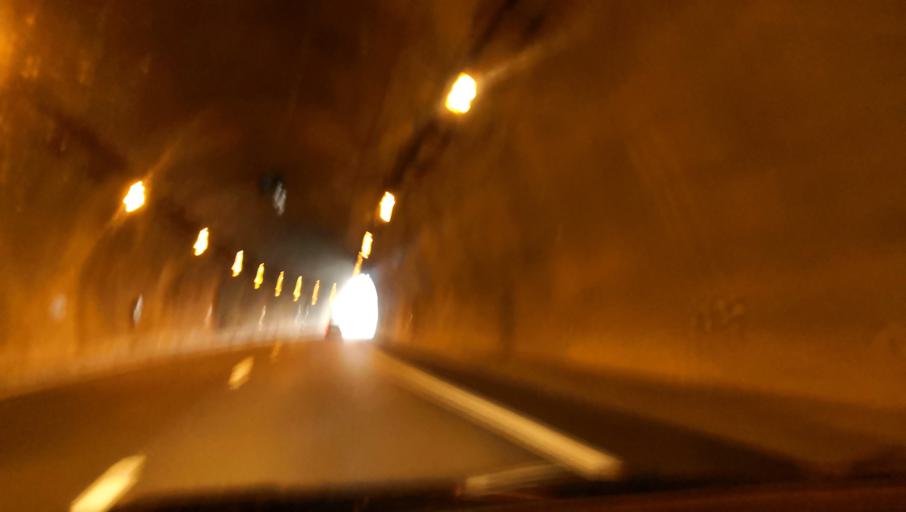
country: PT
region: Viseu
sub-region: Lamego
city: Lamego
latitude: 41.1209
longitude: -7.7787
